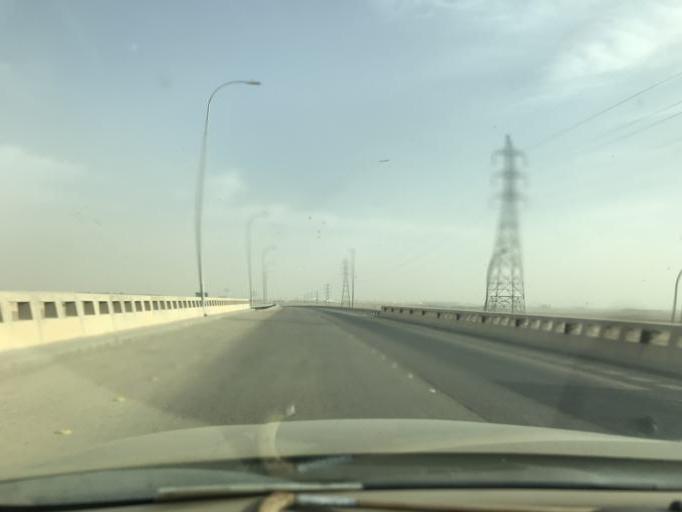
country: SA
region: Ar Riyad
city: Riyadh
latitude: 24.9025
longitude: 46.7061
